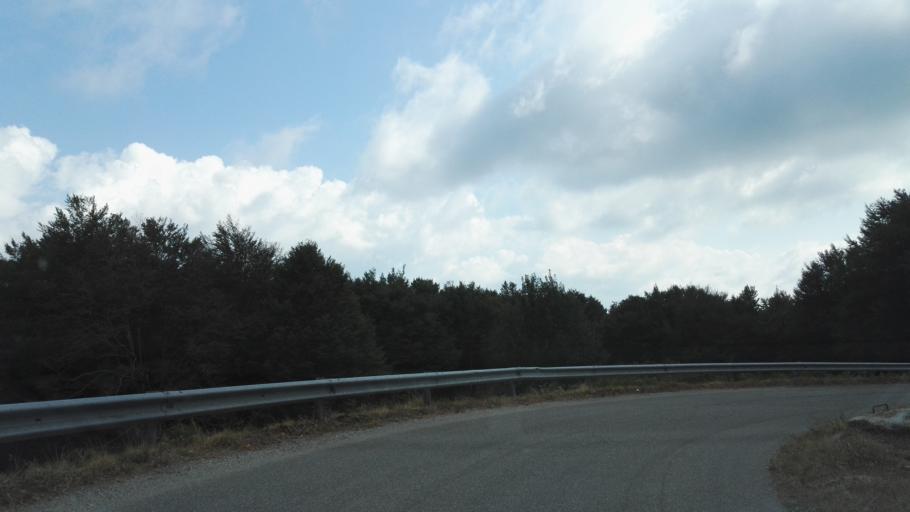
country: IT
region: Calabria
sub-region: Provincia di Vibo-Valentia
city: Nardodipace
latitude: 38.4907
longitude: 16.3458
